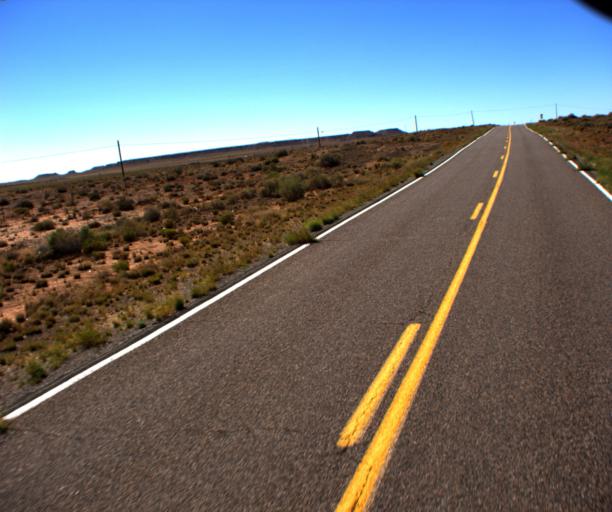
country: US
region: Arizona
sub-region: Coconino County
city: LeChee
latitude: 35.0992
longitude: -110.8624
